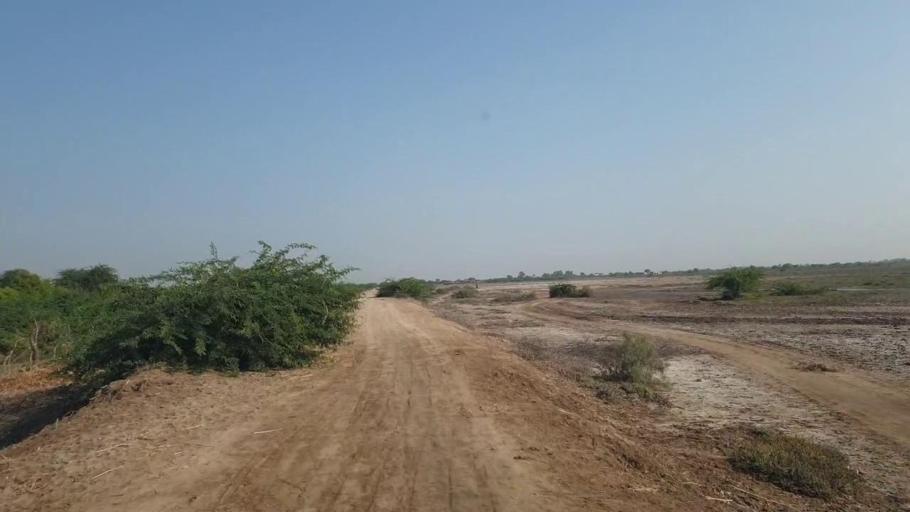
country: PK
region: Sindh
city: Badin
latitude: 24.4573
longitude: 68.7354
